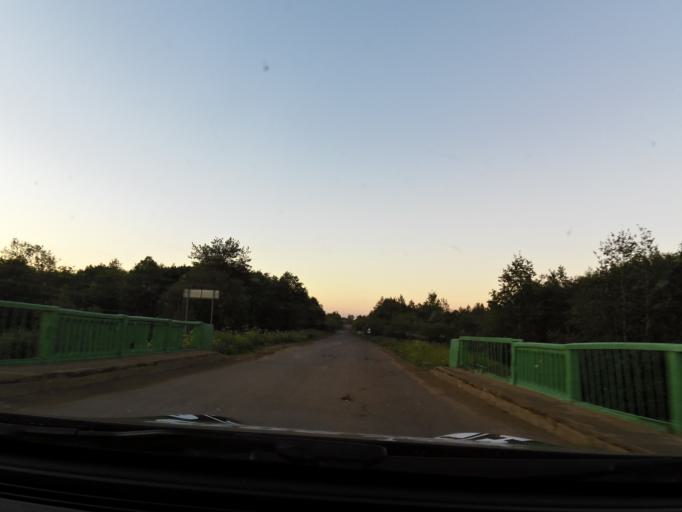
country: RU
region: Leningrad
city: Voznesen'ye
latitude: 60.8357
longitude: 35.7628
